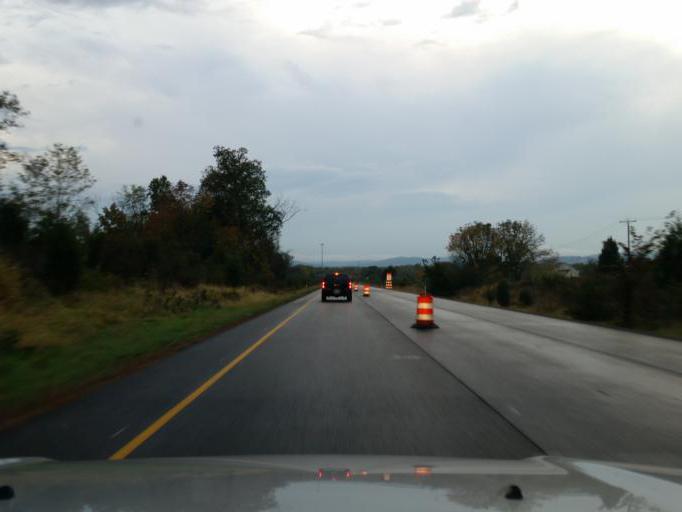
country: US
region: Pennsylvania
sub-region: Adams County
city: Gettysburg
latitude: 39.7678
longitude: -77.2524
